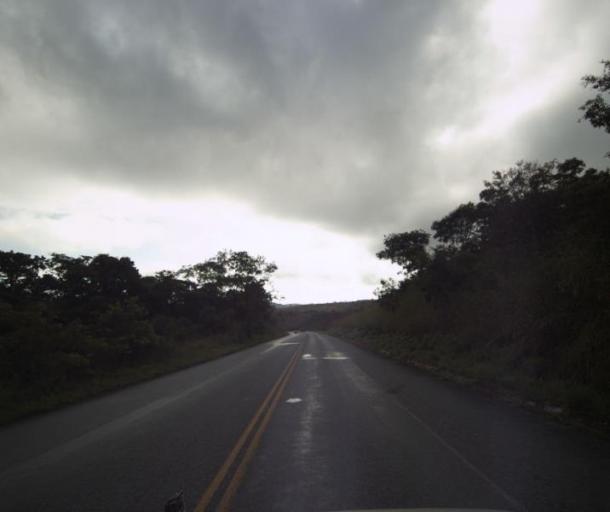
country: BR
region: Goias
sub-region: Pirenopolis
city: Pirenopolis
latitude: -15.7226
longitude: -48.7002
